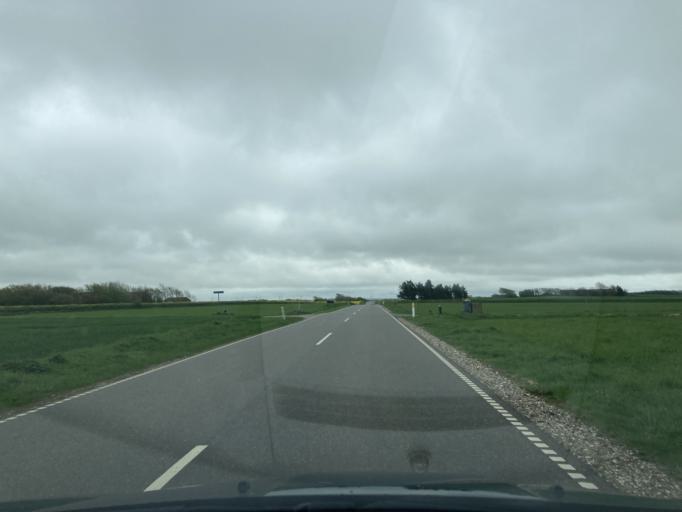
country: DK
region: North Denmark
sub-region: Thisted Kommune
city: Hurup
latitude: 56.8369
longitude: 8.3610
